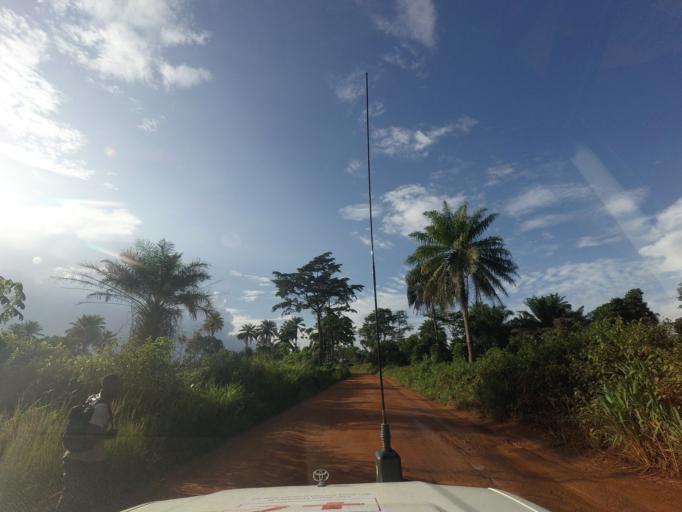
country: GN
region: Nzerekore
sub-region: Nzerekore Prefecture
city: Nzerekore
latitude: 7.7105
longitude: -8.8196
